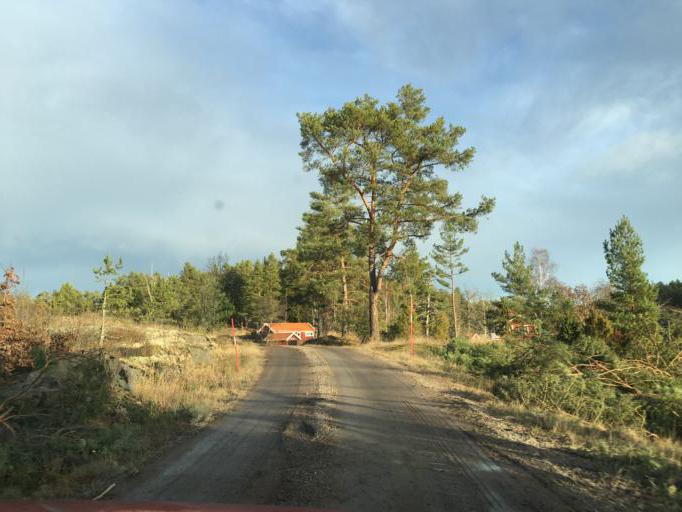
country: SE
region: Kalmar
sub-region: Vasterviks Kommun
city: Vaestervik
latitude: 57.6250
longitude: 16.5615
